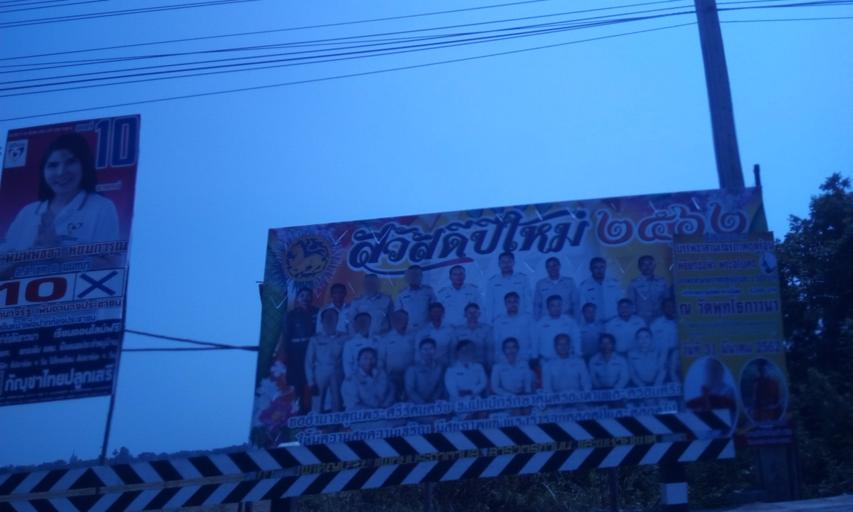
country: TH
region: Nonthaburi
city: Bang Yai
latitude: 13.9097
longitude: 100.3454
